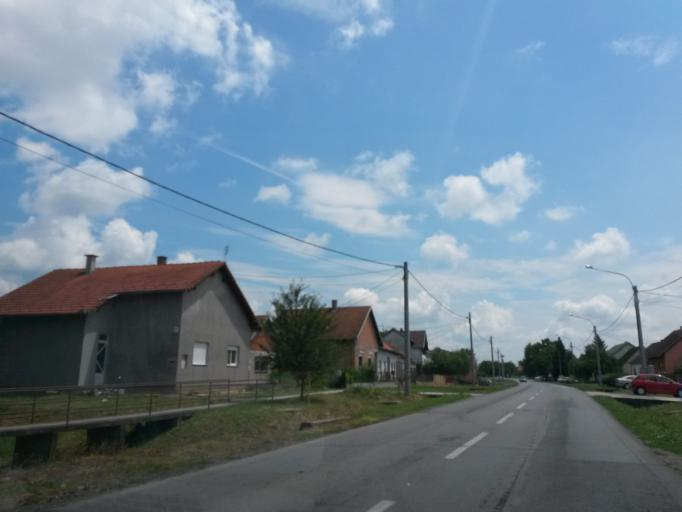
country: HR
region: Osjecko-Baranjska
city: Sarvas
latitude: 45.5222
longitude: 18.8450
